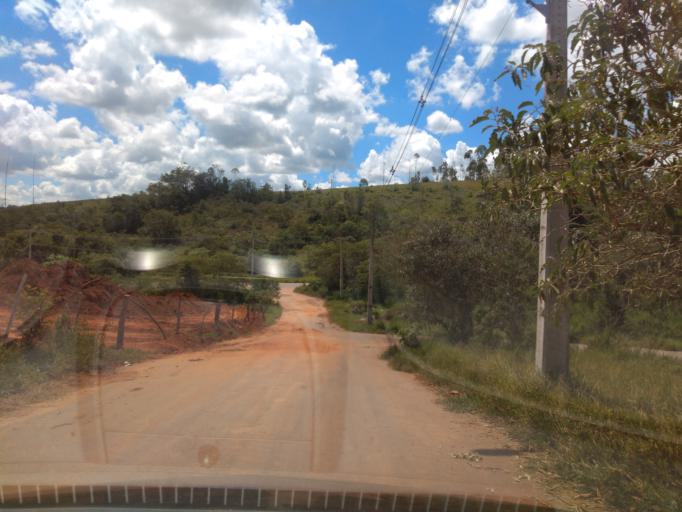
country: BR
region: Minas Gerais
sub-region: Tres Coracoes
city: Tres Coracoes
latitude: -21.6807
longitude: -45.2402
